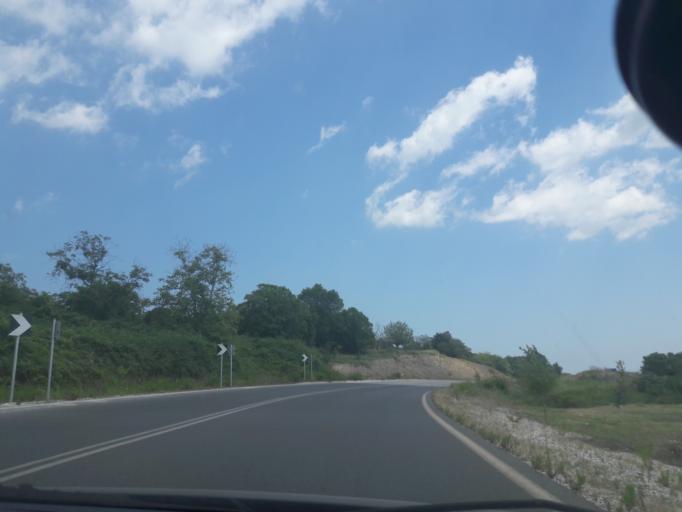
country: GR
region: Central Macedonia
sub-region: Nomos Chalkidikis
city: Polygyros
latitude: 40.3763
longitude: 23.5227
